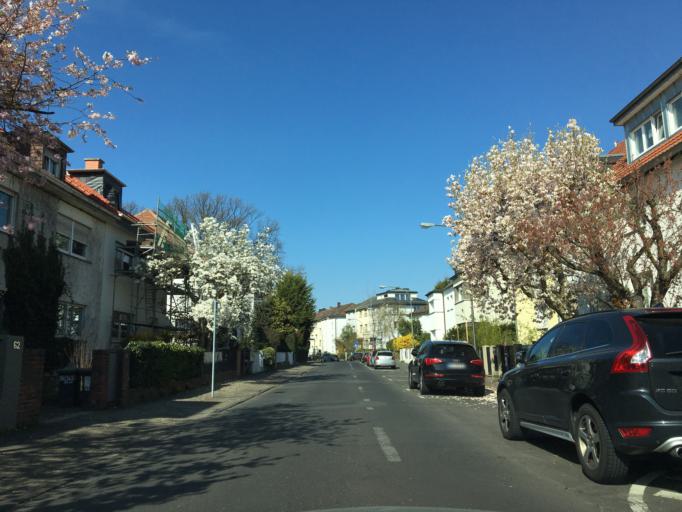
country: DE
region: Hesse
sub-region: Regierungsbezirk Darmstadt
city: Frankfurt am Main
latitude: 50.1503
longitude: 8.6566
